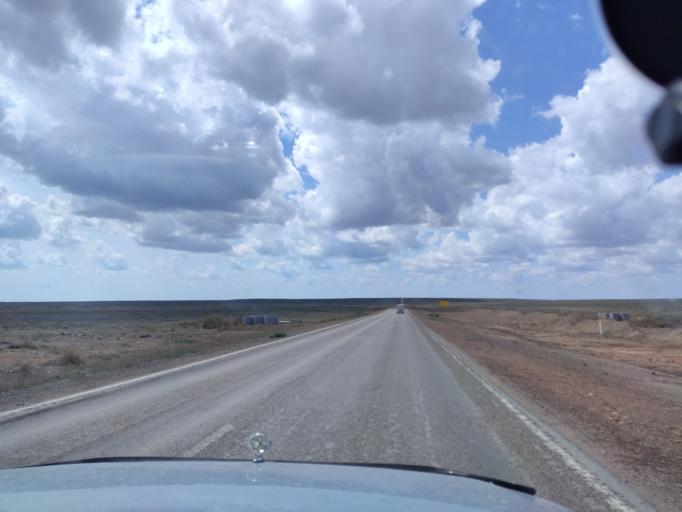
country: KZ
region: Qaraghandy
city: Saryshaghan
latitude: 46.0017
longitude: 73.5804
